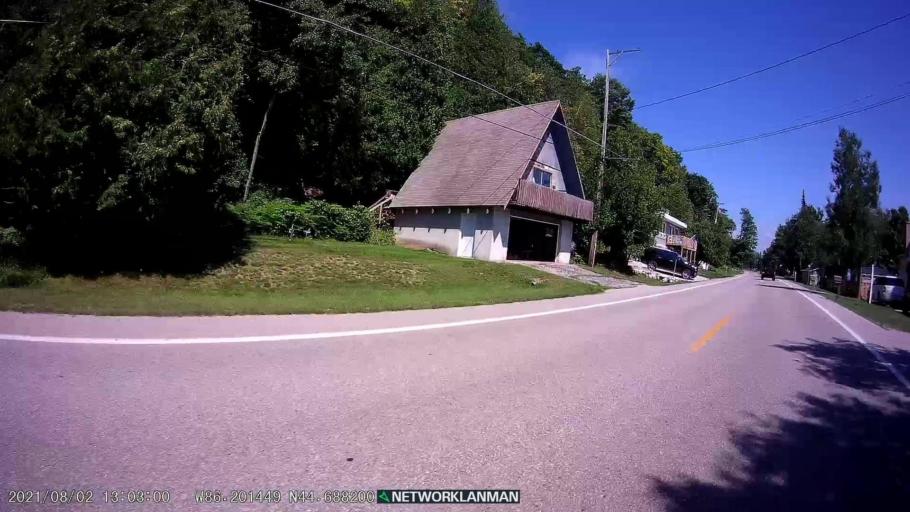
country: US
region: Michigan
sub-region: Benzie County
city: Frankfort
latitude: 44.6882
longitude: -86.2011
